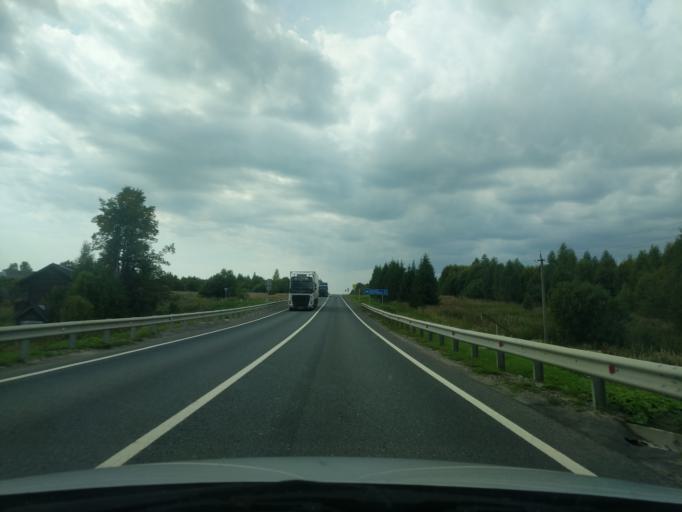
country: RU
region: Kostroma
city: Manturovo
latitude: 58.1633
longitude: 44.4000
